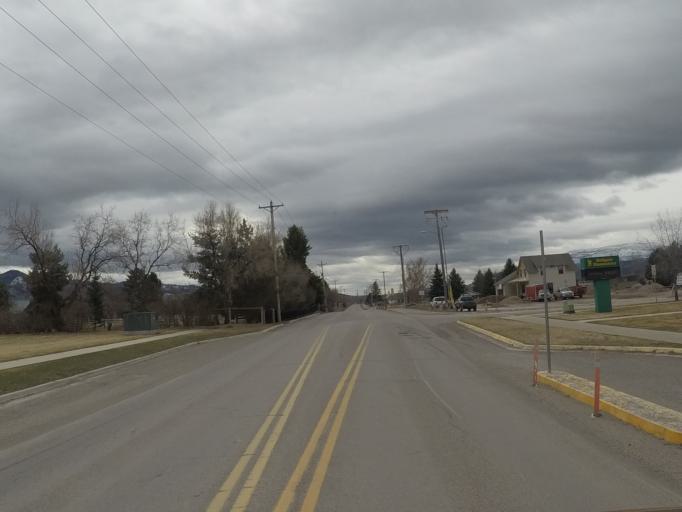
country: US
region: Montana
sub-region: Missoula County
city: Orchard Homes
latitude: 46.8928
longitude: -114.0553
